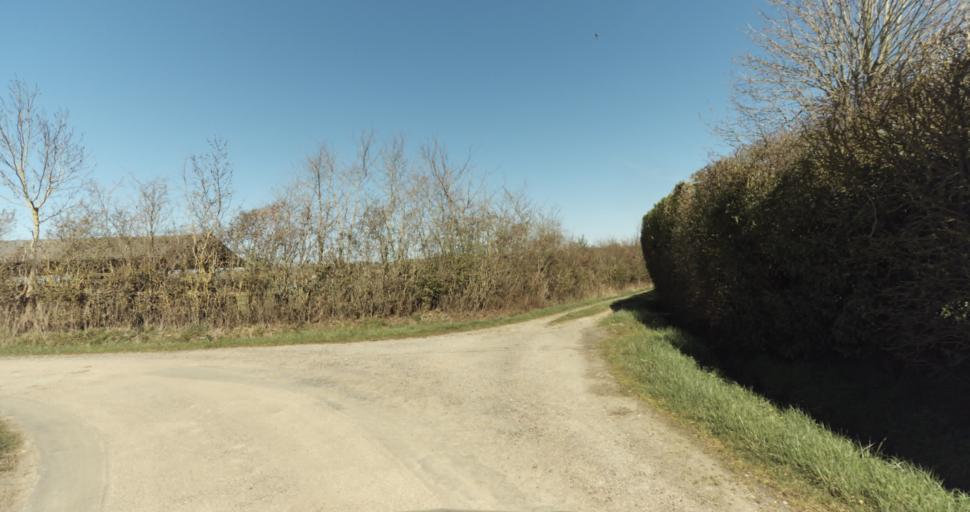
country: FR
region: Lower Normandy
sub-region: Departement du Calvados
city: Saint-Pierre-sur-Dives
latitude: 49.0333
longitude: 0.0195
